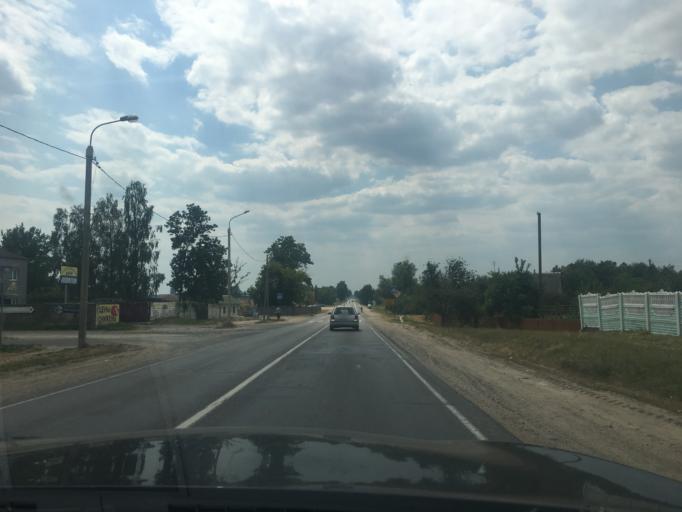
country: BY
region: Brest
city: Pruzhany
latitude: 52.5518
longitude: 24.4712
